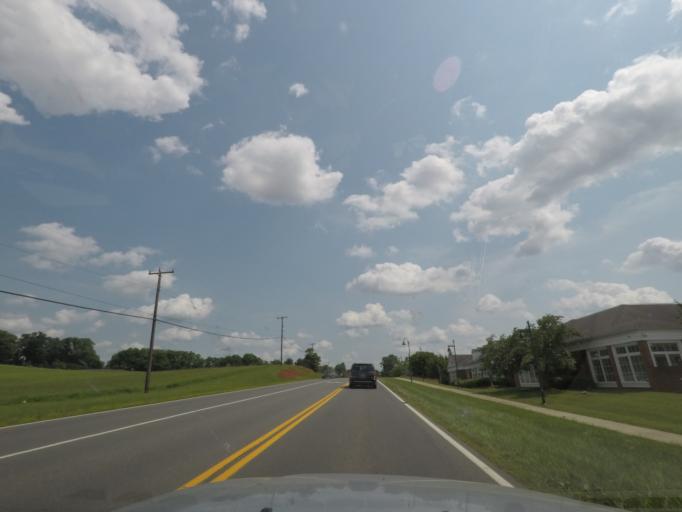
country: US
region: Virginia
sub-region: Orange County
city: Orange
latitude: 38.2602
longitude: -78.1170
